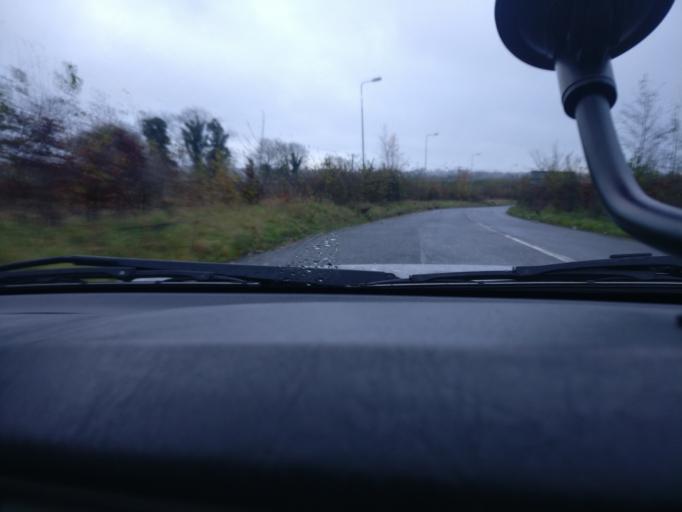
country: IE
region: Leinster
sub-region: An Iarmhi
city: Kinnegad
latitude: 53.4526
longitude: -7.1234
